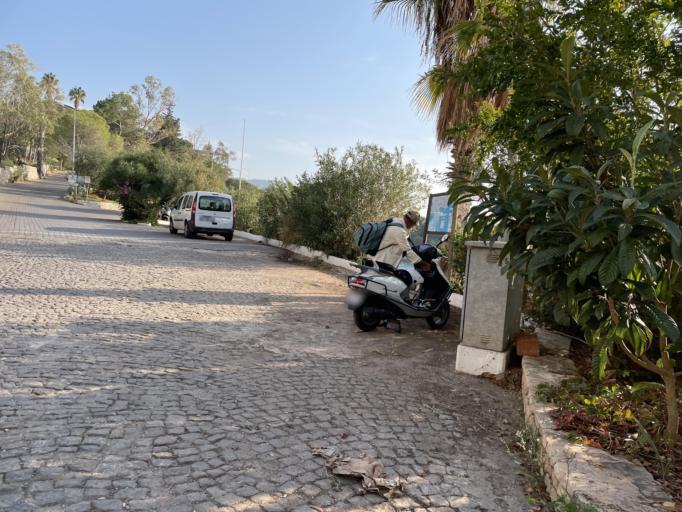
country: TR
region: Antalya
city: Kas
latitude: 36.1963
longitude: 29.6459
